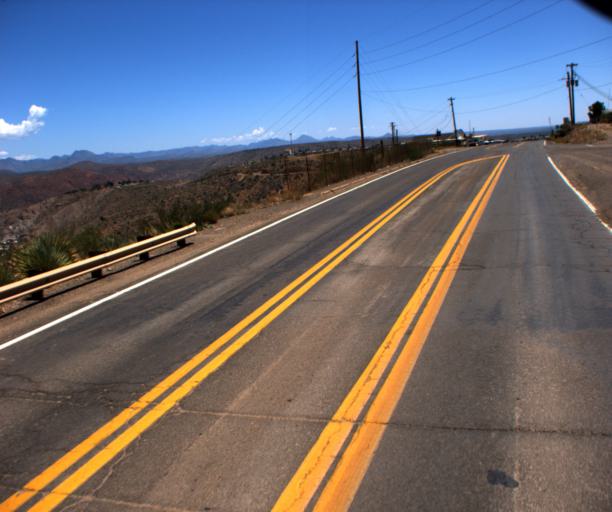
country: US
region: Arizona
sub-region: Greenlee County
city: Clifton
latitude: 33.0576
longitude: -109.3293
